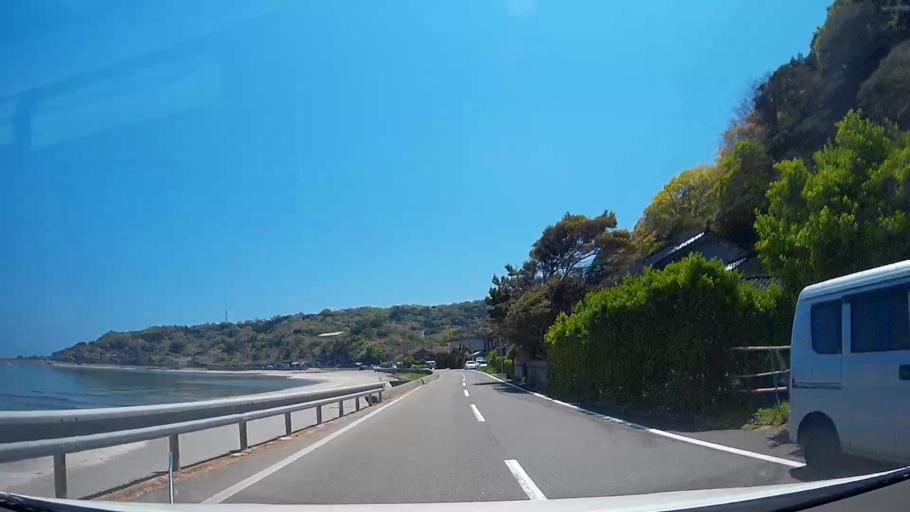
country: JP
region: Ishikawa
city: Nanao
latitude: 37.5281
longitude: 137.2788
